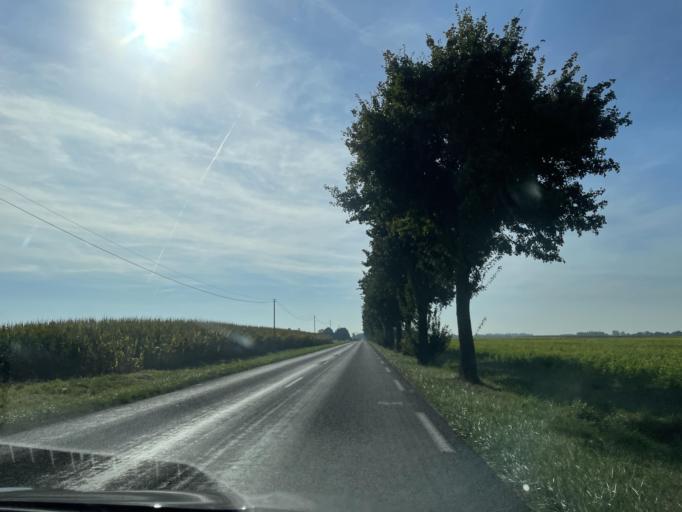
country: FR
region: Ile-de-France
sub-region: Departement de Seine-et-Marne
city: Coulommiers
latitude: 48.8619
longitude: 3.0912
